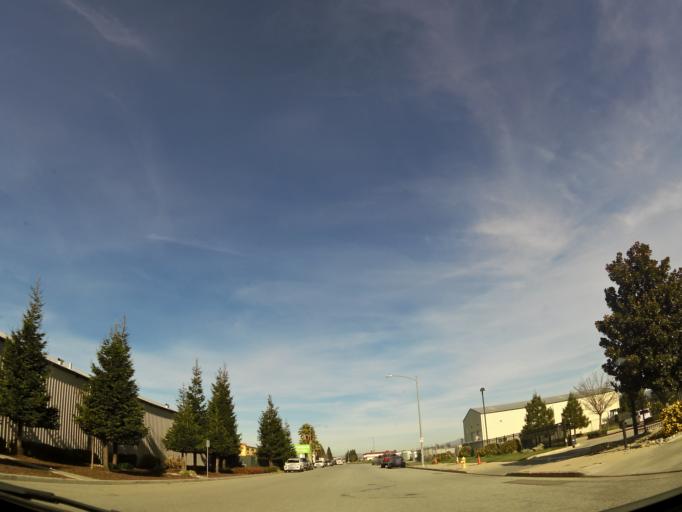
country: US
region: California
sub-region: Santa Clara County
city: Gilroy
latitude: 37.0226
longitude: -121.5728
